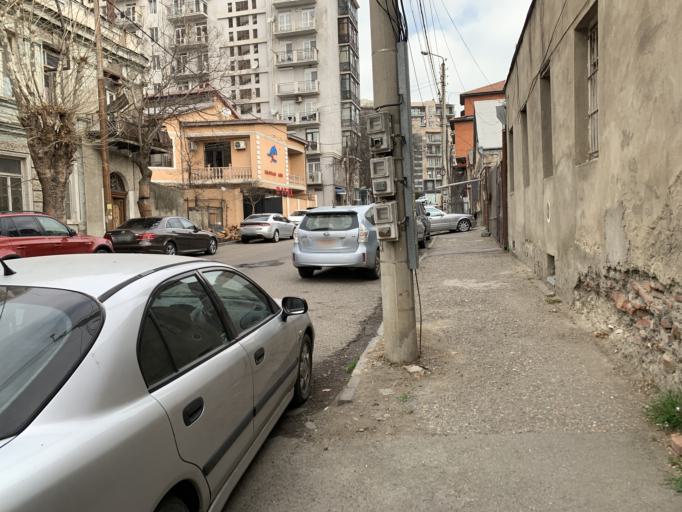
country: GE
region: T'bilisi
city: Tbilisi
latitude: 41.6801
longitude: 44.8389
